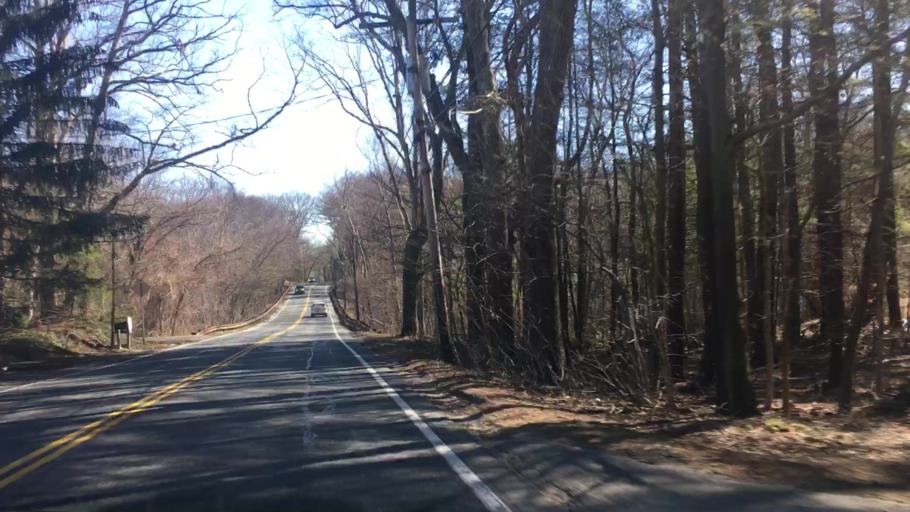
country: US
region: Massachusetts
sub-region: Middlesex County
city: Sherborn
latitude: 42.2523
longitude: -71.3598
